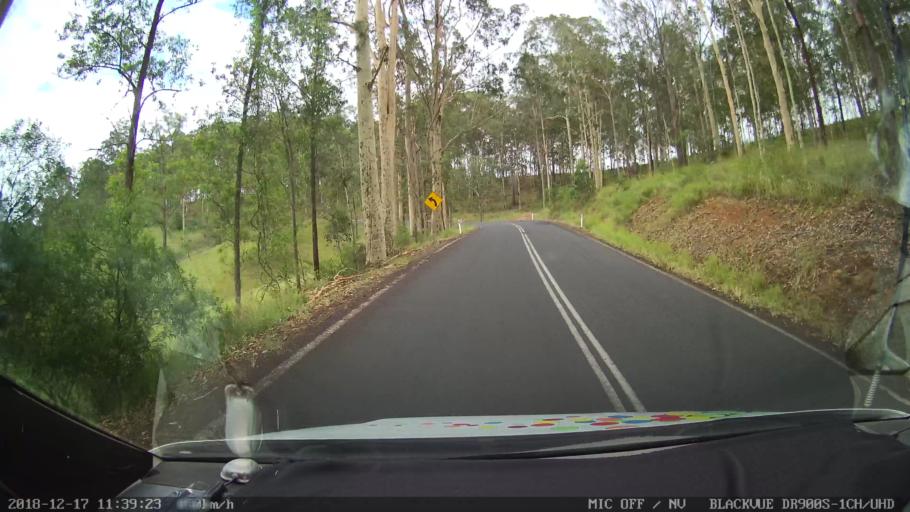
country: AU
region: New South Wales
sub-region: Kyogle
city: Kyogle
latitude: -28.6878
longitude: 152.5948
